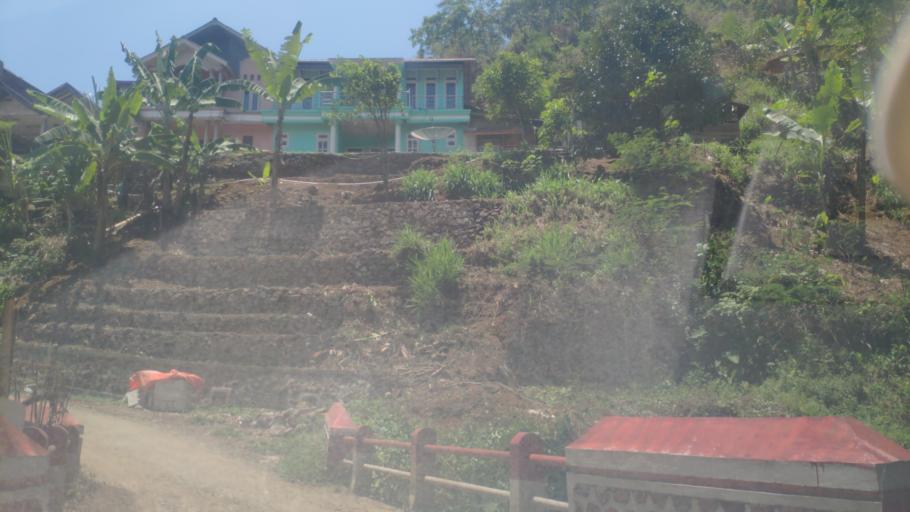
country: ID
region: Central Java
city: Buaran
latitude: -7.2750
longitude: 109.5929
